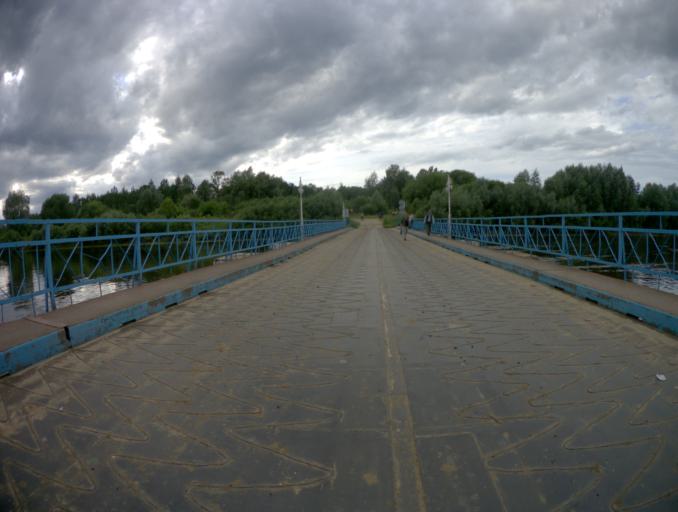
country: RU
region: Vladimir
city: Gorokhovets
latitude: 56.2097
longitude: 42.6792
